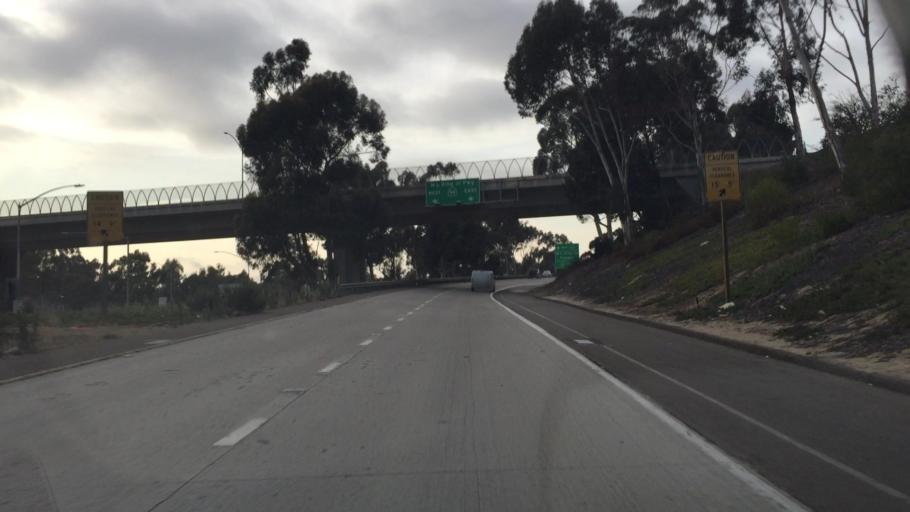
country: US
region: California
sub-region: San Diego County
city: National City
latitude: 32.7143
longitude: -117.1019
